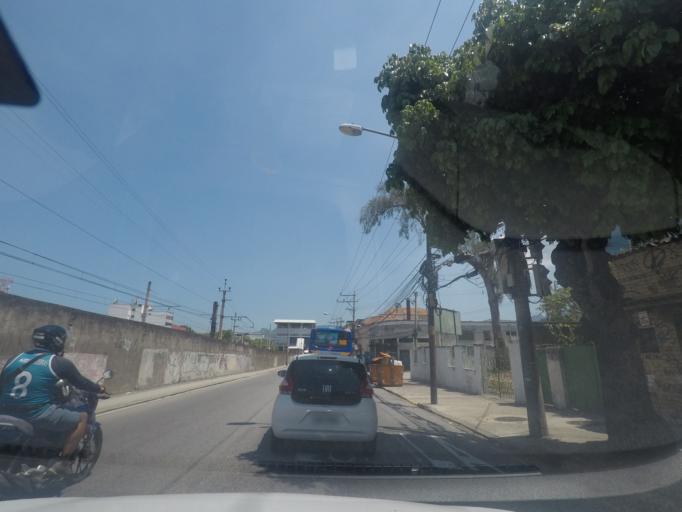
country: BR
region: Rio de Janeiro
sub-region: Rio De Janeiro
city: Rio de Janeiro
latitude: -22.8650
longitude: -43.2564
